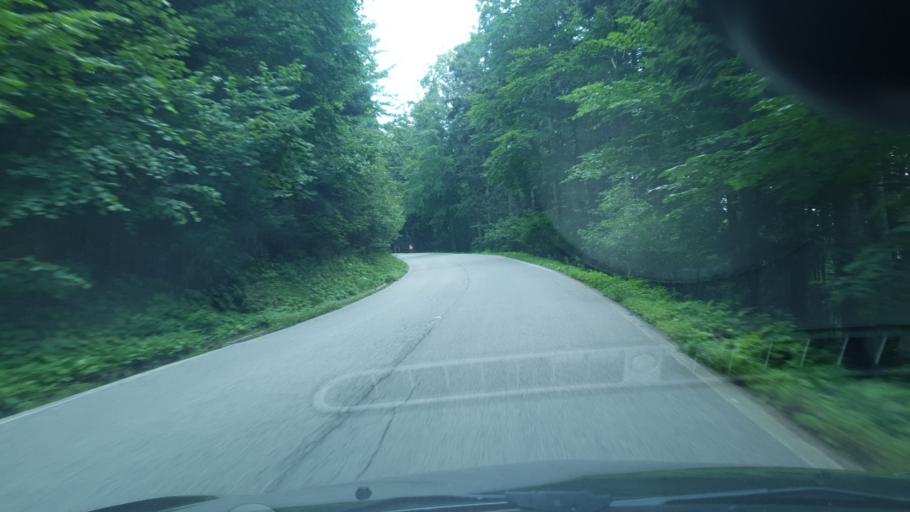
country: HR
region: Grad Zagreb
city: Kasina
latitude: 45.9052
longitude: 15.9673
